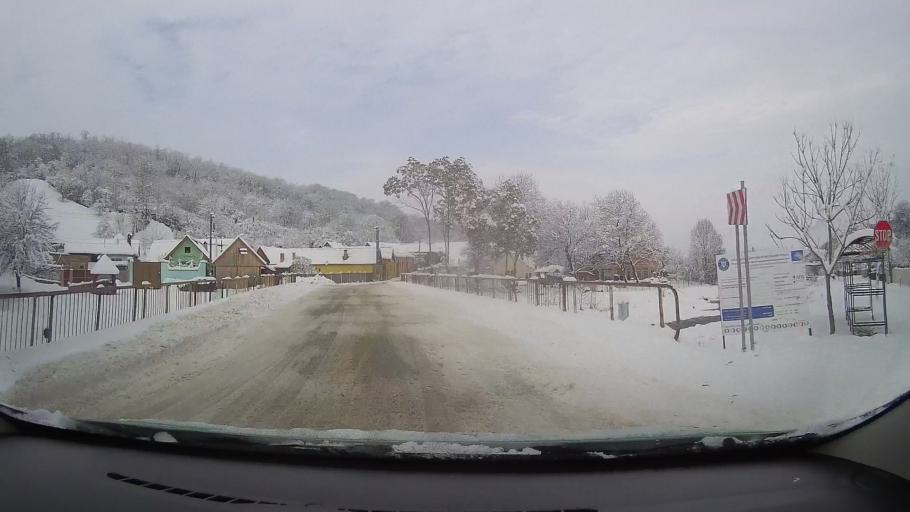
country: RO
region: Alba
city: Pianu de Sus
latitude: 45.8901
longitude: 23.4864
